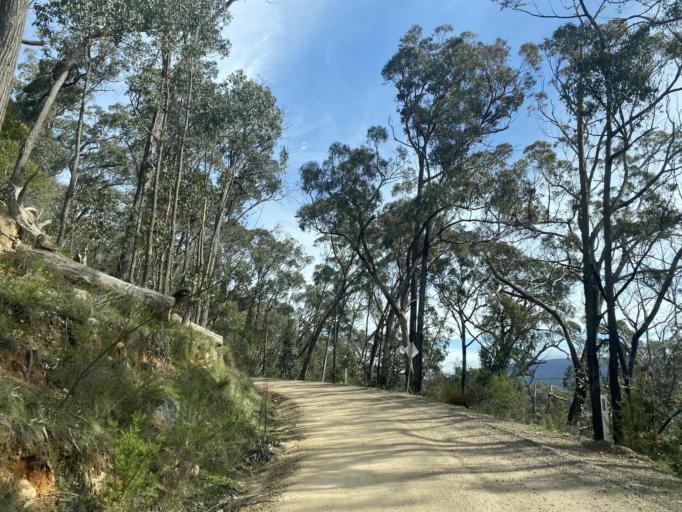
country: AU
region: Victoria
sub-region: Mansfield
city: Mansfield
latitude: -36.8384
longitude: 146.1649
